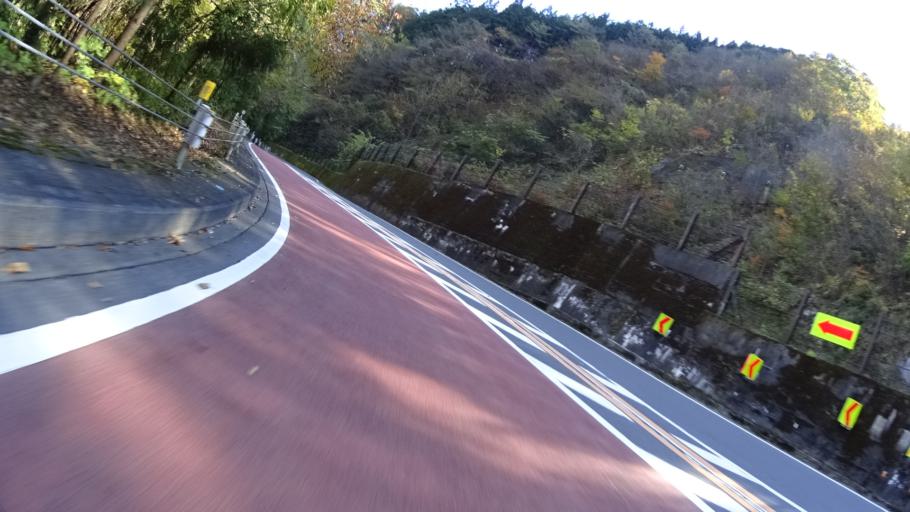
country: JP
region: Yamanashi
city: Uenohara
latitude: 35.7274
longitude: 139.0404
